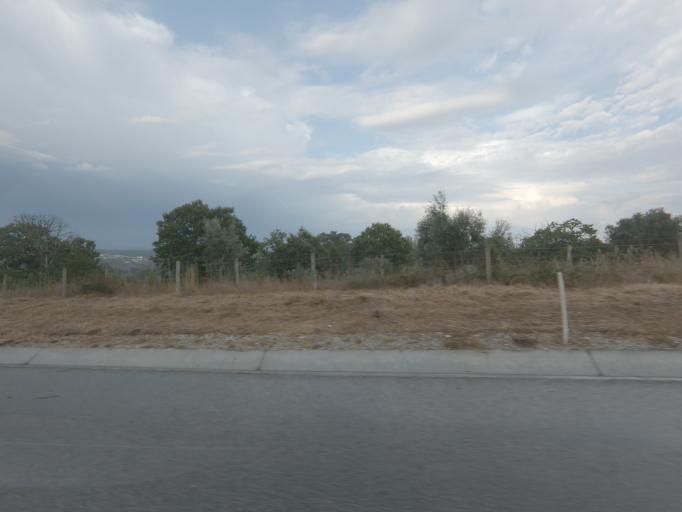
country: PT
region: Viseu
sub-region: Viseu
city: Campo
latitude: 40.7350
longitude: -7.9230
